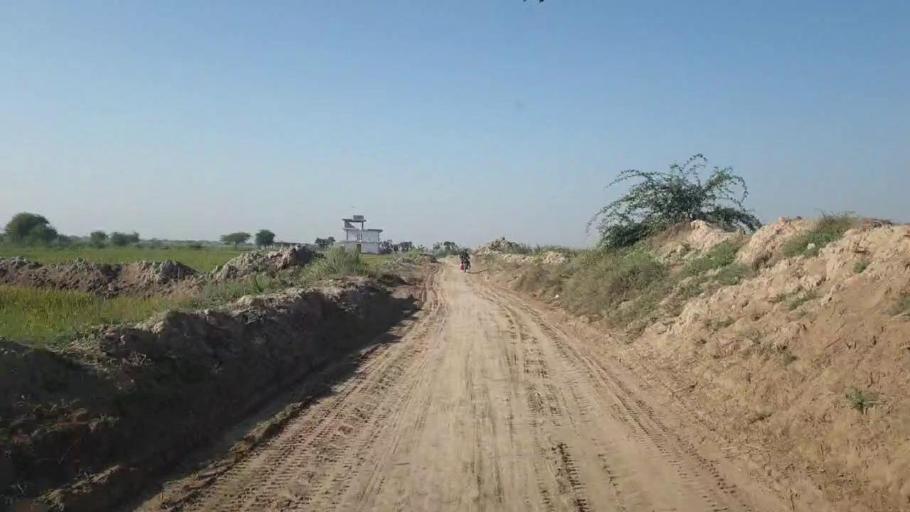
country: PK
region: Sindh
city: Badin
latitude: 24.7096
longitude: 68.7825
